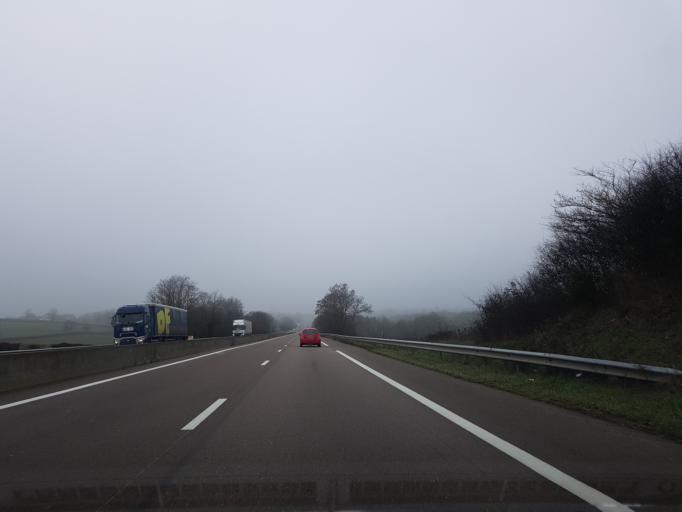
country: FR
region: Bourgogne
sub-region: Departement de Saone-et-Loire
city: Ecuisses
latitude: 46.7457
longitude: 4.5232
